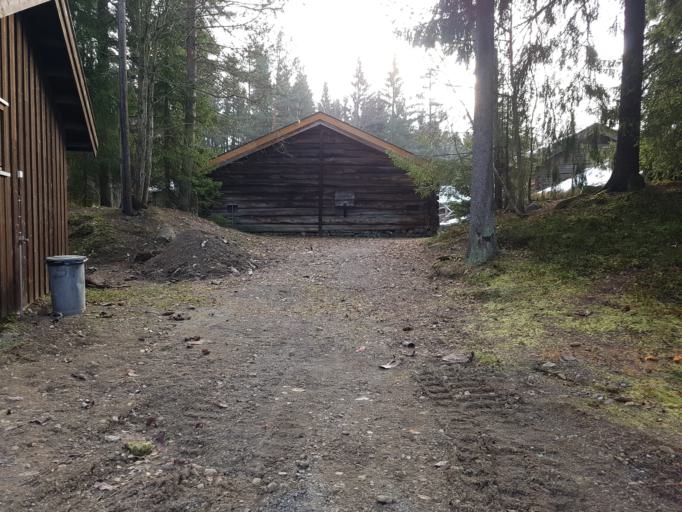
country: NO
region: Oppland
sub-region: Lillehammer
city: Lillehammer
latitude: 61.1123
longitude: 10.4822
